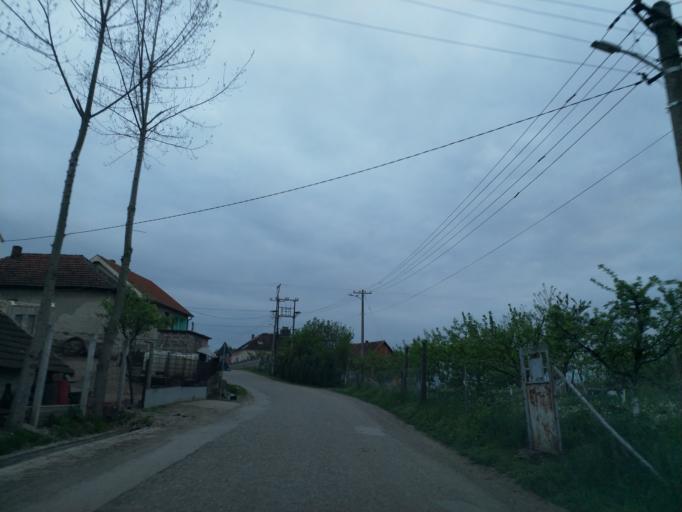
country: RS
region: Central Serbia
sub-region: Pomoravski Okrug
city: Paracin
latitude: 43.9452
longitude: 21.4947
